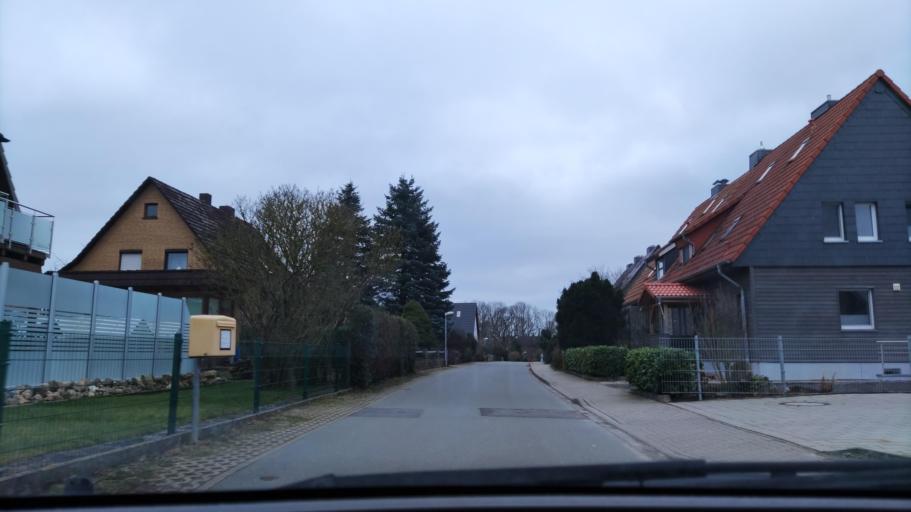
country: DE
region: Lower Saxony
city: Reppenstedt
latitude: 53.2485
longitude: 10.3647
